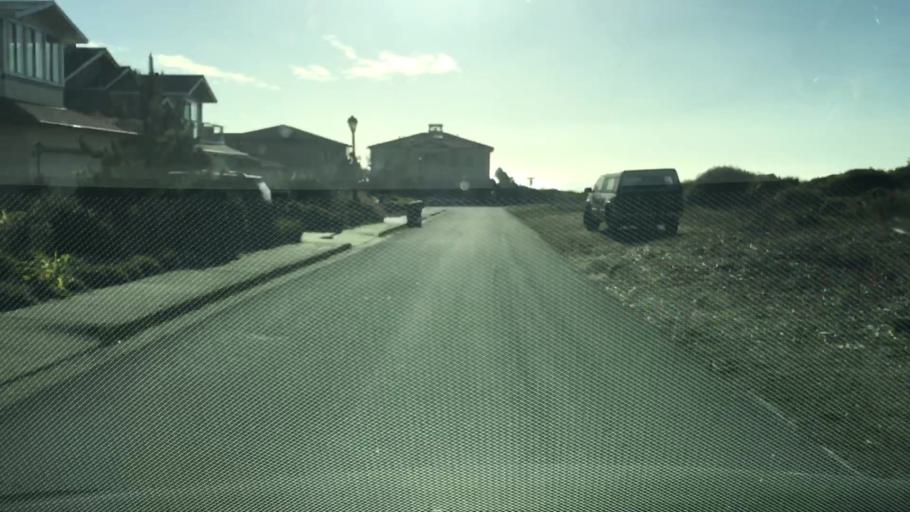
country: US
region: California
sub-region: San Mateo County
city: Half Moon Bay
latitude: 37.4782
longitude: -122.4458
